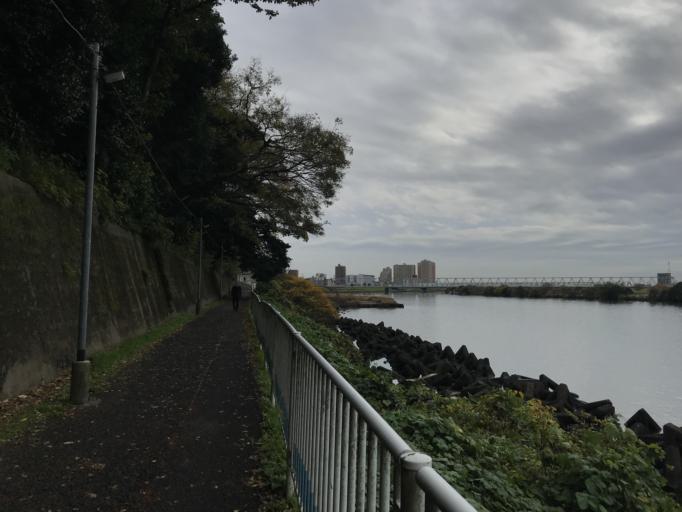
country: JP
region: Chiba
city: Matsudo
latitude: 35.7436
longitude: 139.9006
